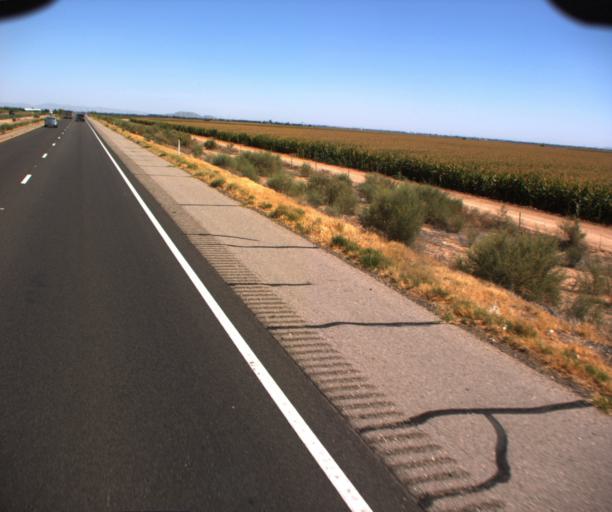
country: US
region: Arizona
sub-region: Pinal County
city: Maricopa
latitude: 33.0106
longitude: -112.0478
